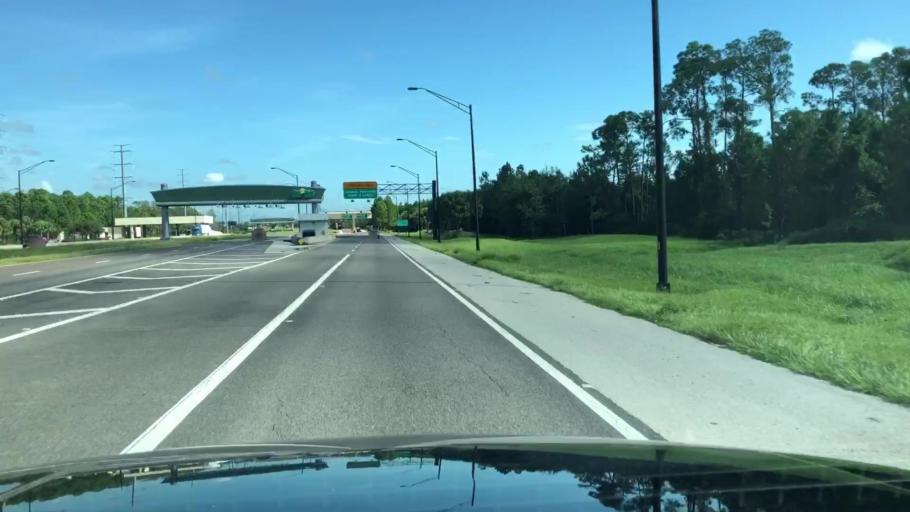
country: US
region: Florida
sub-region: Polk County
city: Citrus Ridge
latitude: 28.3563
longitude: -81.6128
